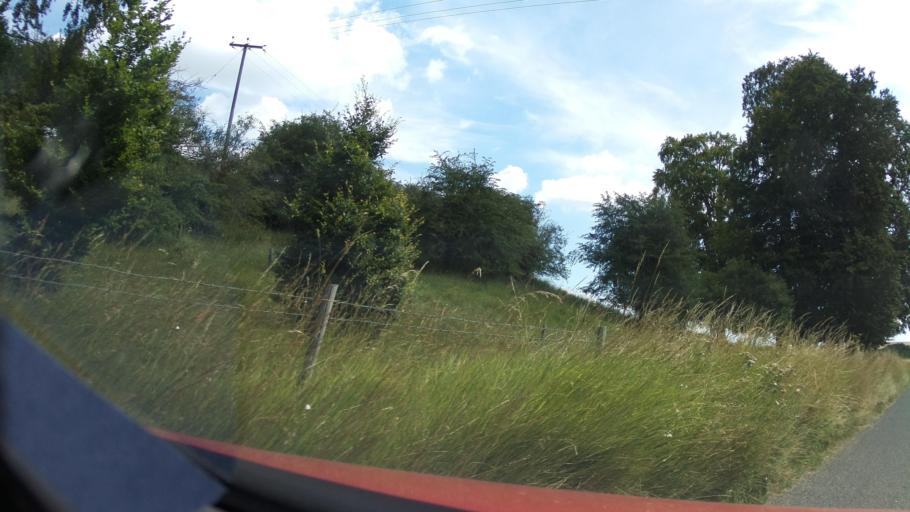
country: GB
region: England
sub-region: Wiltshire
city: Aldbourne
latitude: 51.5292
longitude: -1.5862
